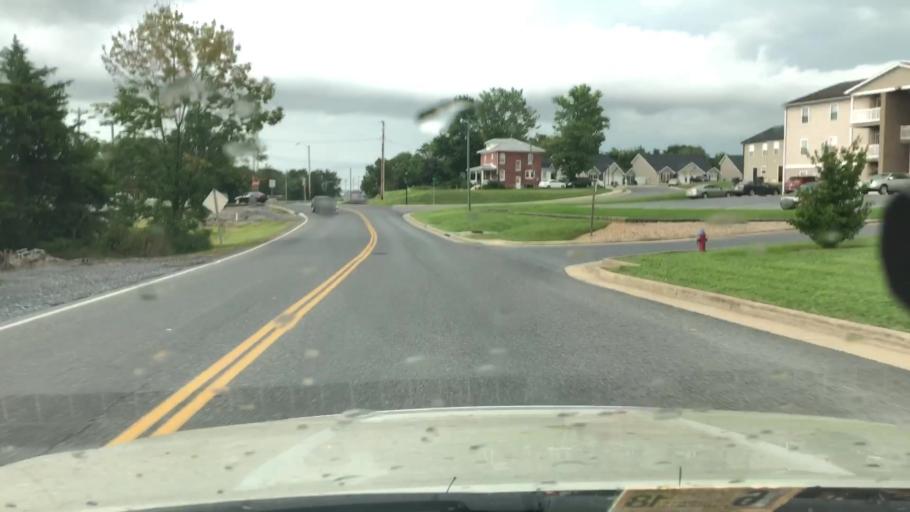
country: US
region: Virginia
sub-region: City of Harrisonburg
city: Harrisonburg
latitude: 38.4328
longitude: -78.8990
